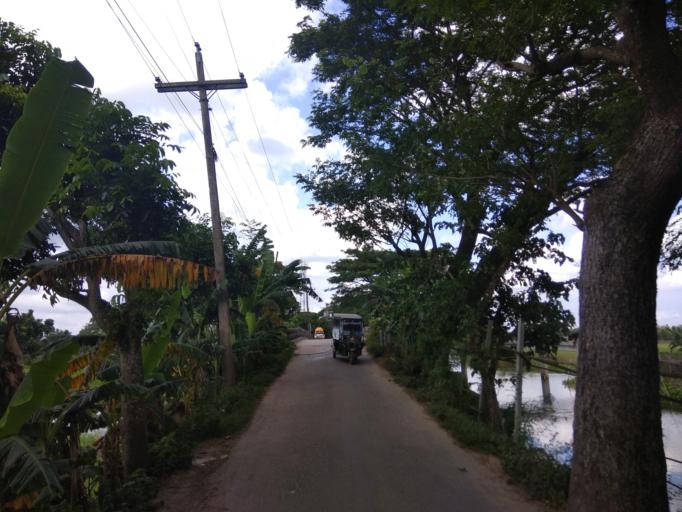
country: BD
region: Dhaka
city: Narayanganj
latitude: 23.4732
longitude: 90.4577
